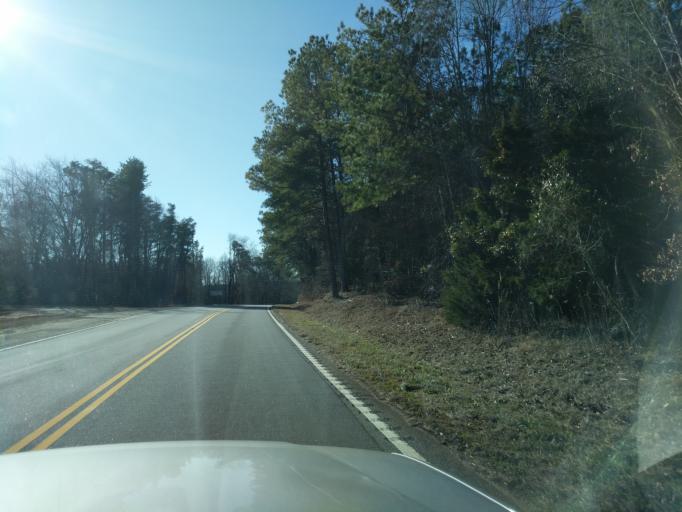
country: US
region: South Carolina
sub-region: Anderson County
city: Homeland Park
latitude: 34.4210
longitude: -82.7548
